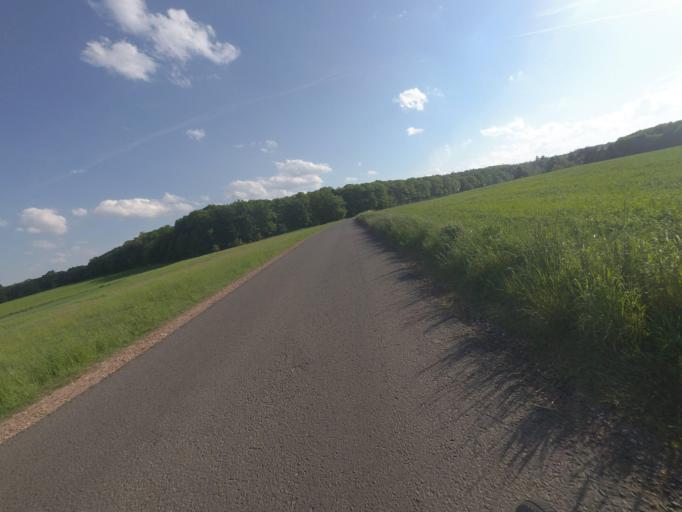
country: DE
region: Rheinland-Pfalz
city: Kirchheimbolanden
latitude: 49.6675
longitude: 7.9850
